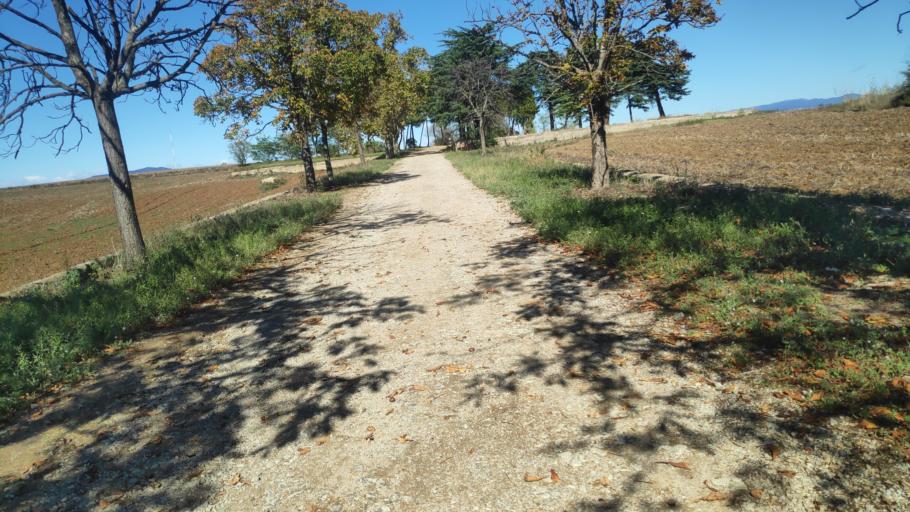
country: ES
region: Catalonia
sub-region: Provincia de Barcelona
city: Mollet del Valles
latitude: 41.5389
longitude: 2.2006
